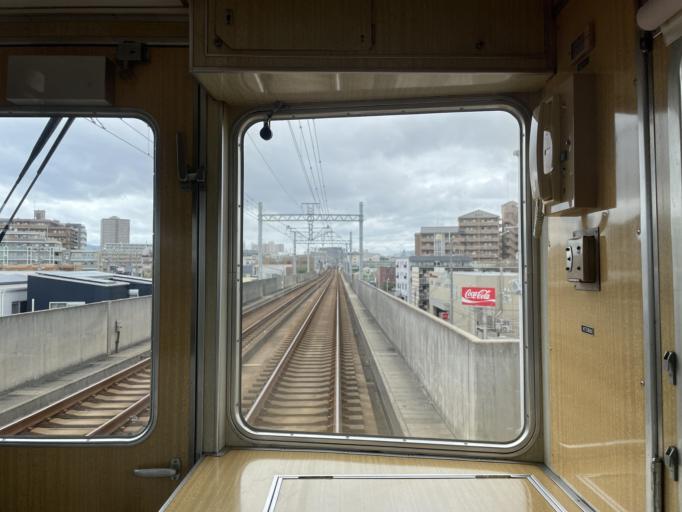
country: JP
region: Hyogo
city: Nishinomiya-hama
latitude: 34.7346
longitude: 135.3532
